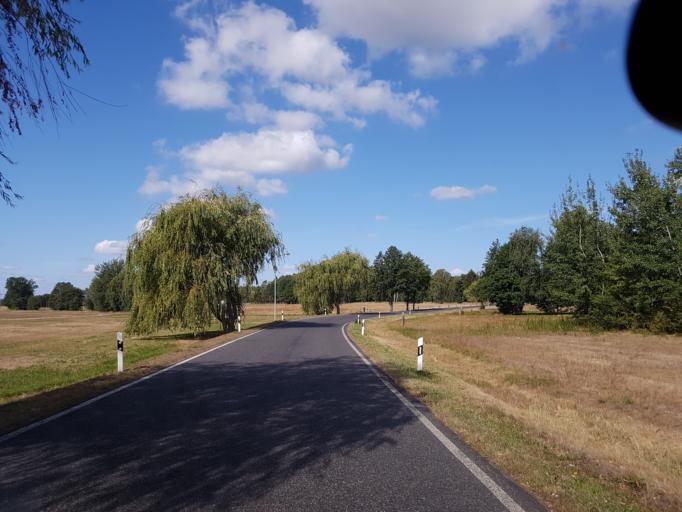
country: DE
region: Brandenburg
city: Sonnewalde
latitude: 51.7356
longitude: 13.6277
